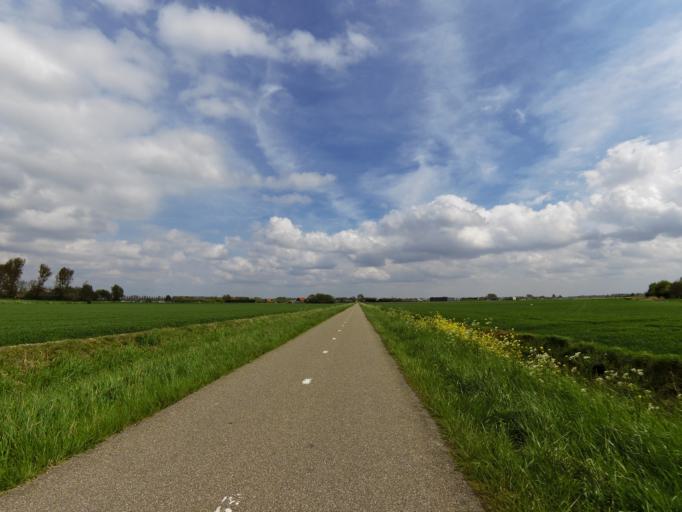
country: NL
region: South Holland
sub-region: Gemeente Hellevoetsluis
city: Nieuwenhoorn
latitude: 51.8257
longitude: 4.2317
